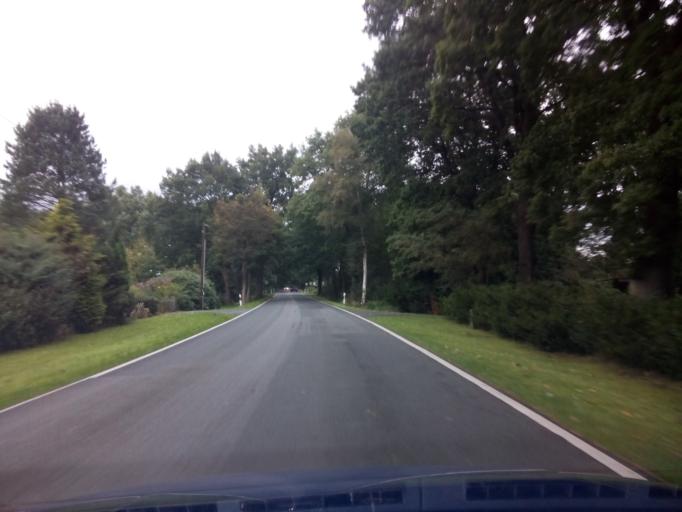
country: DE
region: Lower Saxony
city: Beverstedt
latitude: 53.4675
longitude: 8.8479
